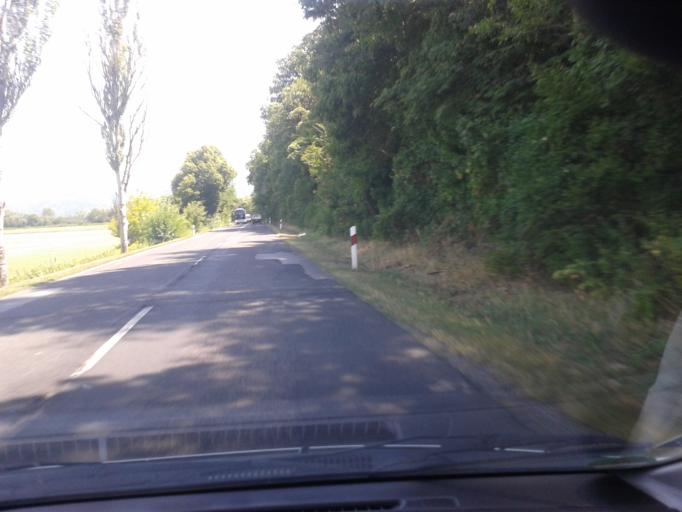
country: HU
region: Pest
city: Szob
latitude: 47.8101
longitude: 18.8375
